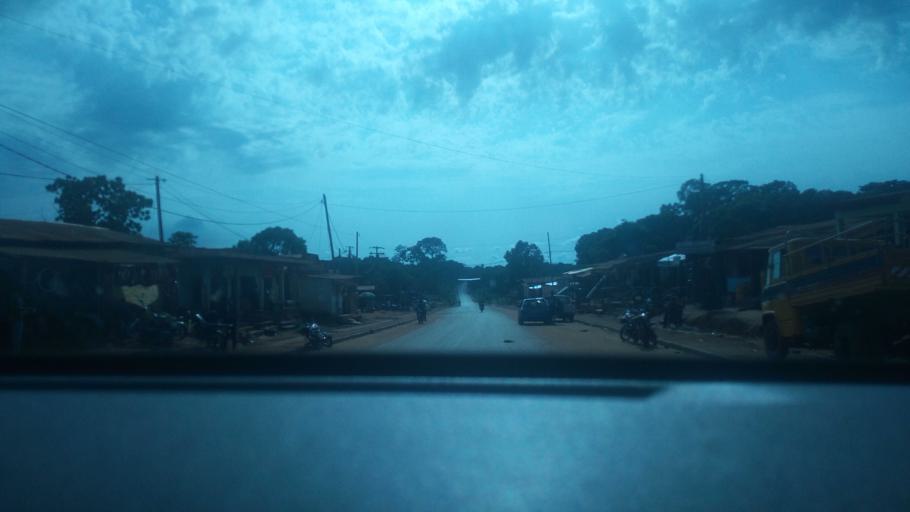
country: CM
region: Centre
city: Nkoteng
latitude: 4.5048
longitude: 12.1191
